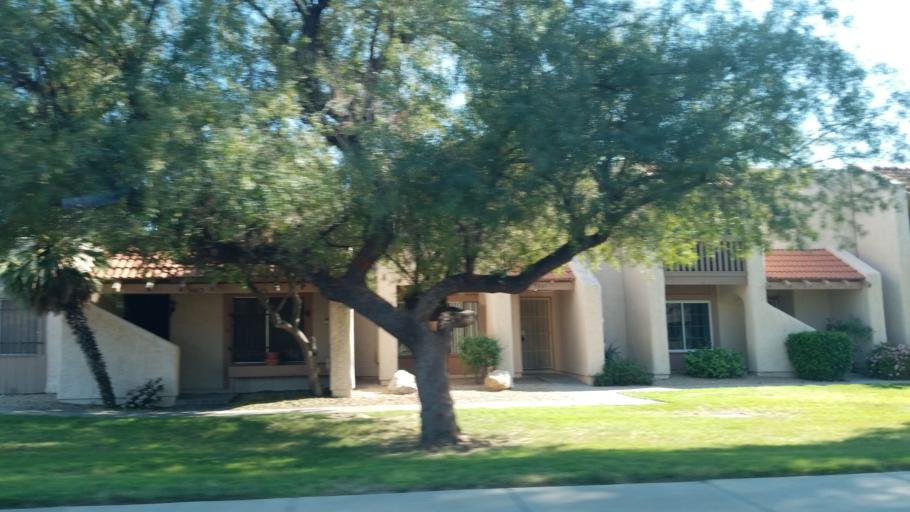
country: US
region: Arizona
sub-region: Maricopa County
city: Glendale
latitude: 33.5603
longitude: -112.1756
